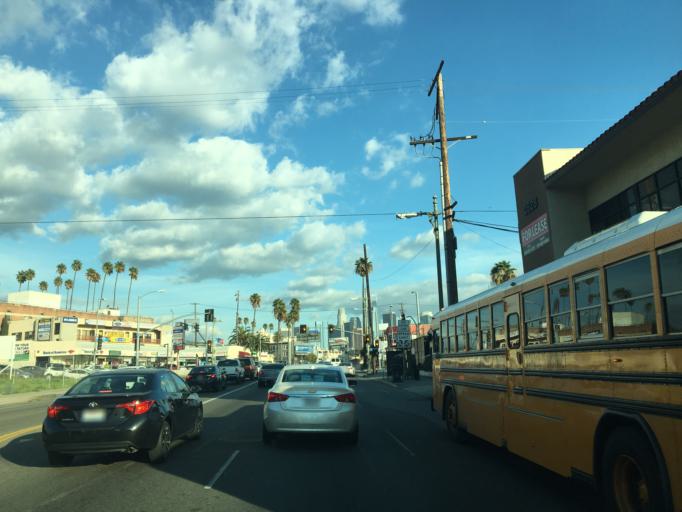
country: US
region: California
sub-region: Los Angeles County
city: Echo Park
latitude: 34.0524
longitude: -118.2851
